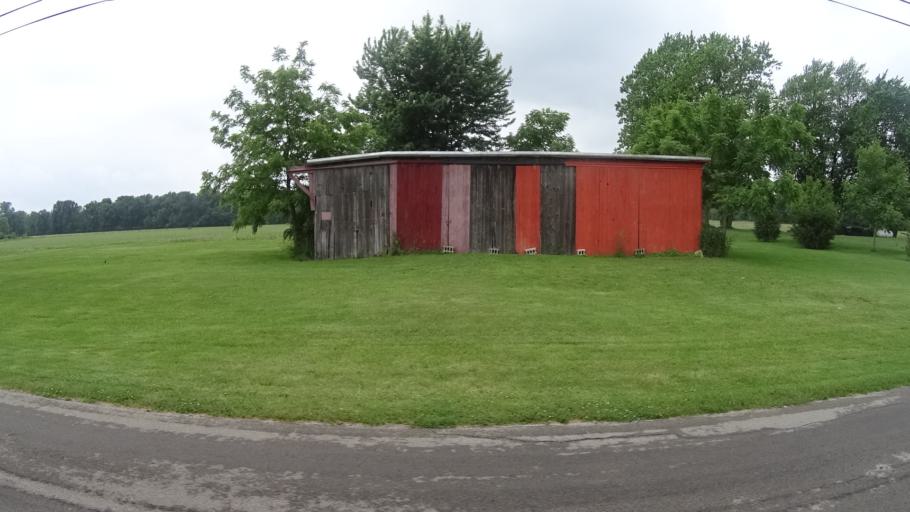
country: US
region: Ohio
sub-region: Huron County
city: Bellevue
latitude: 41.3574
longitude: -82.7731
